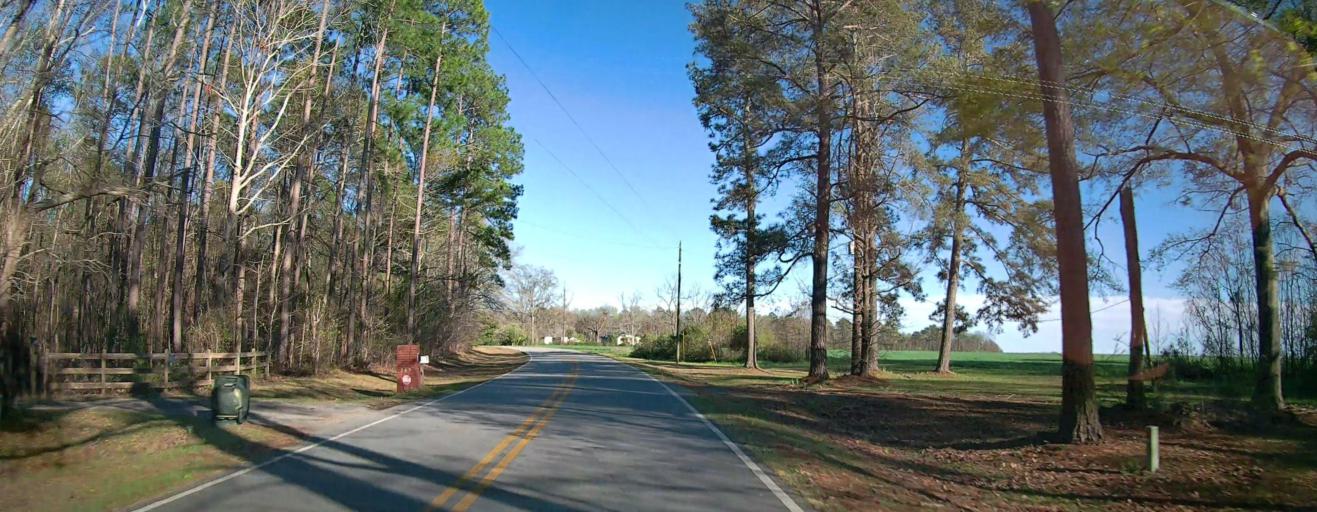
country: US
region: Georgia
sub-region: Houston County
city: Perry
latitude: 32.3617
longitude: -83.6535
